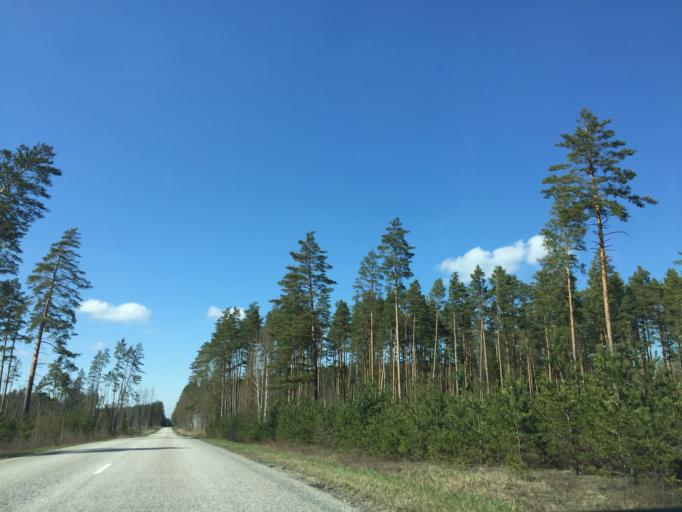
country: LV
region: Strenci
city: Seda
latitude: 57.5893
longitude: 25.7394
